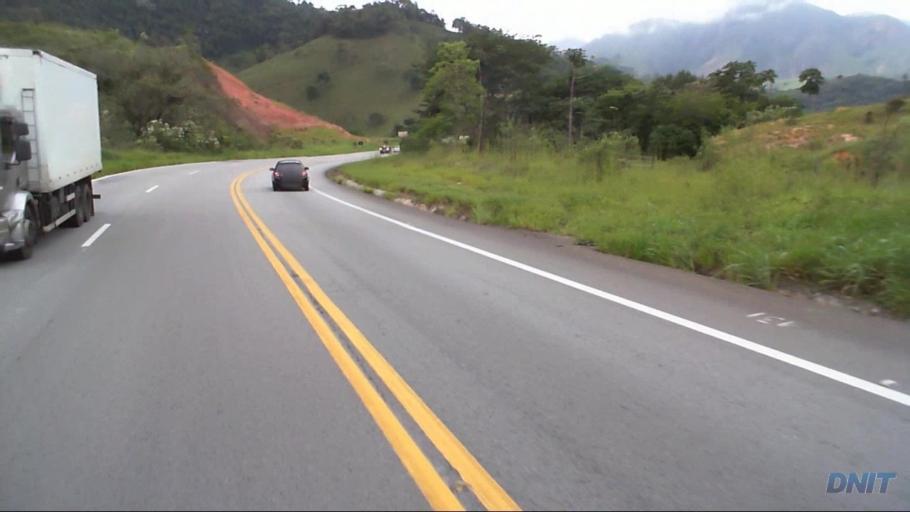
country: BR
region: Minas Gerais
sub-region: Nova Era
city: Nova Era
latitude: -19.6648
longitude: -42.9648
